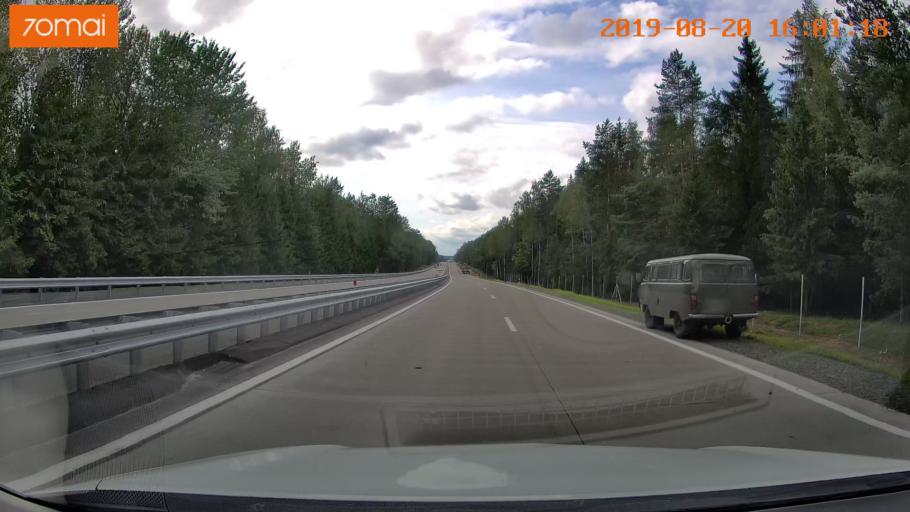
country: BY
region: Minsk
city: Korolev Stan
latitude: 54.0495
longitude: 27.7849
